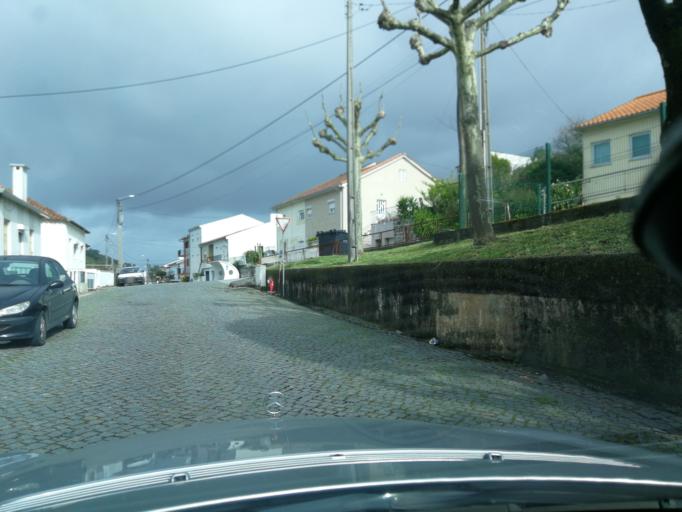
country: PT
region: Braga
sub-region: Braga
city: Braga
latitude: 41.5315
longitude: -8.4076
